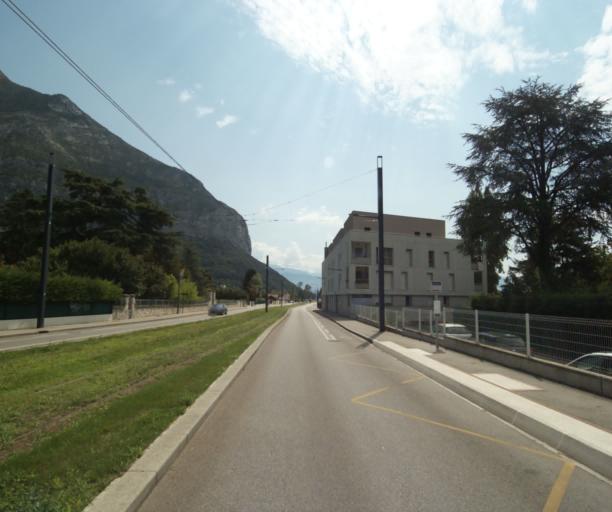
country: FR
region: Rhone-Alpes
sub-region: Departement de l'Isere
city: Saint-Egreve
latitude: 45.2281
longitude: 5.6842
